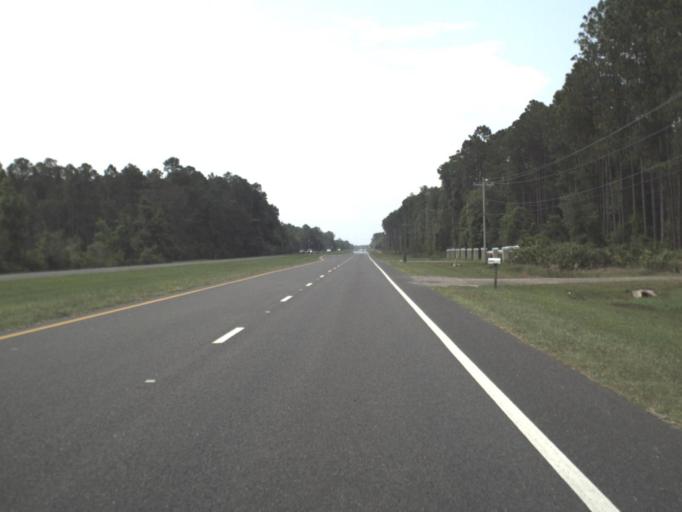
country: US
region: Florida
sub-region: Clay County
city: Green Cove Springs
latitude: 29.8454
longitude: -81.6620
